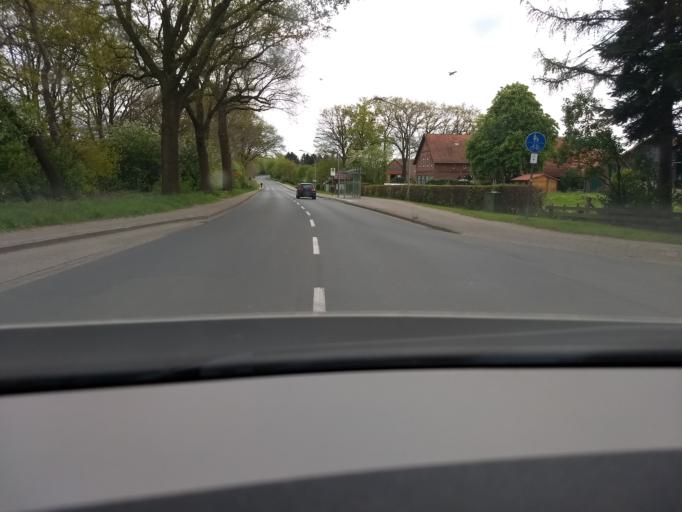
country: DE
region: Lower Saxony
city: Rastede
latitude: 53.2022
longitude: 8.2441
